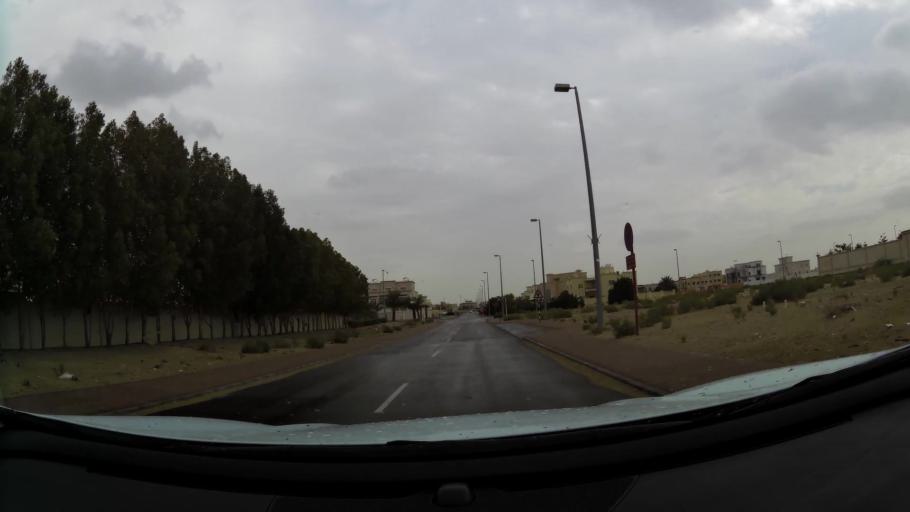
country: AE
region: Abu Dhabi
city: Abu Dhabi
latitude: 24.3621
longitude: 54.6239
